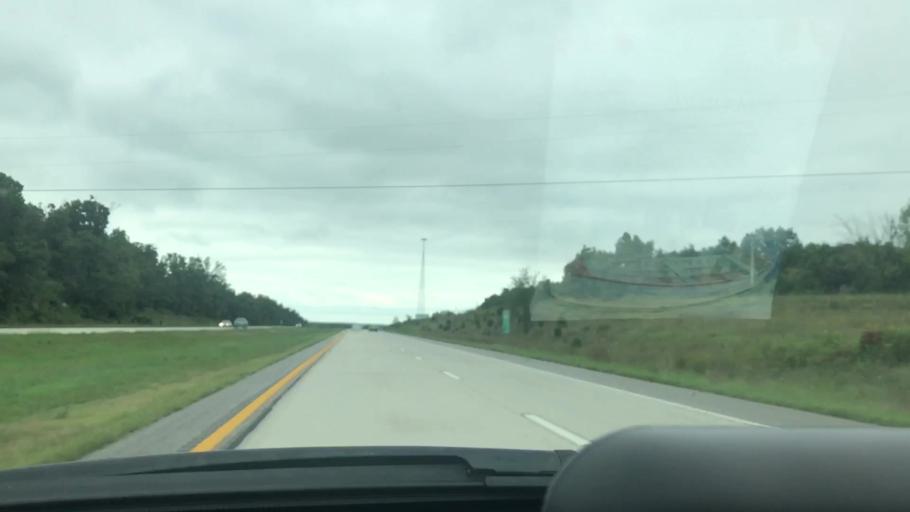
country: US
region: Missouri
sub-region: Greene County
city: Fair Grove
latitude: 37.5028
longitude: -93.1389
